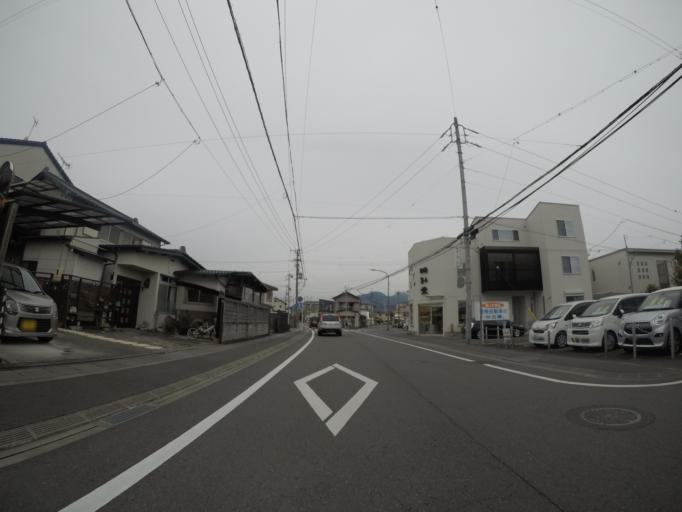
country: JP
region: Shizuoka
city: Shizuoka-shi
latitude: 34.9972
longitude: 138.4178
